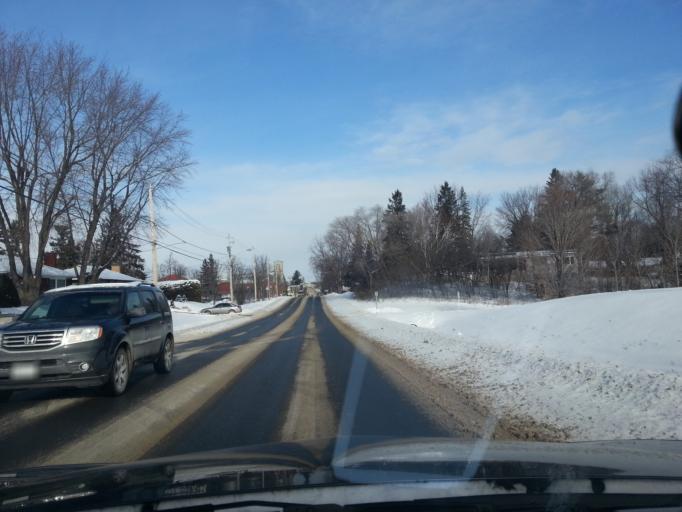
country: CA
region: Ontario
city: Carleton Place
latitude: 45.2197
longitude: -76.1961
